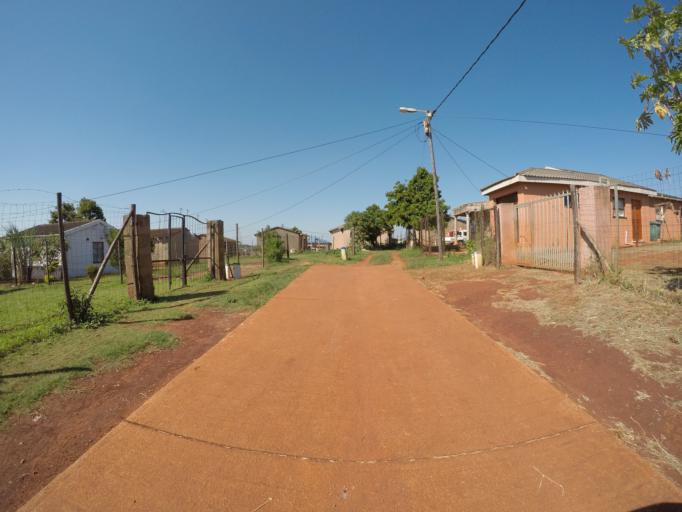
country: ZA
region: KwaZulu-Natal
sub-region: uThungulu District Municipality
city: Empangeni
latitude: -28.7725
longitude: 31.8789
